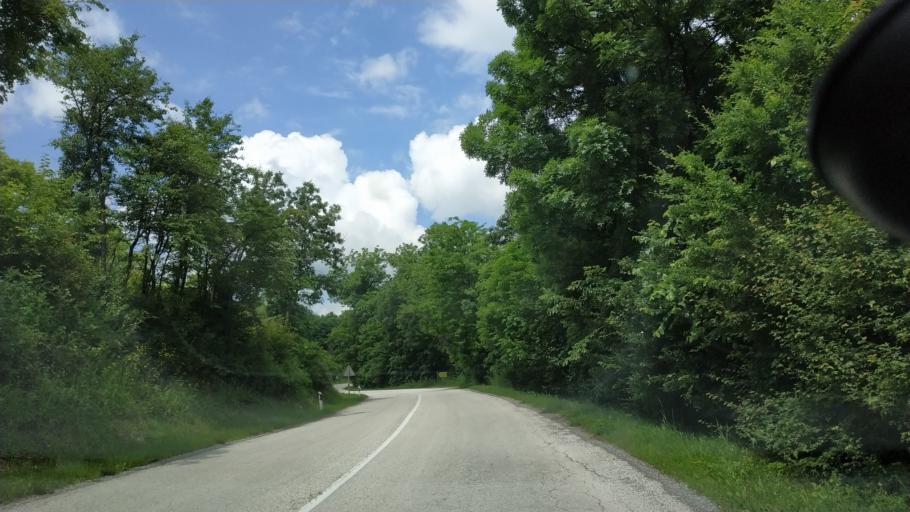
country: RS
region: Central Serbia
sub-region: Borski Okrug
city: Bor
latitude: 44.0618
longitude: 22.0410
